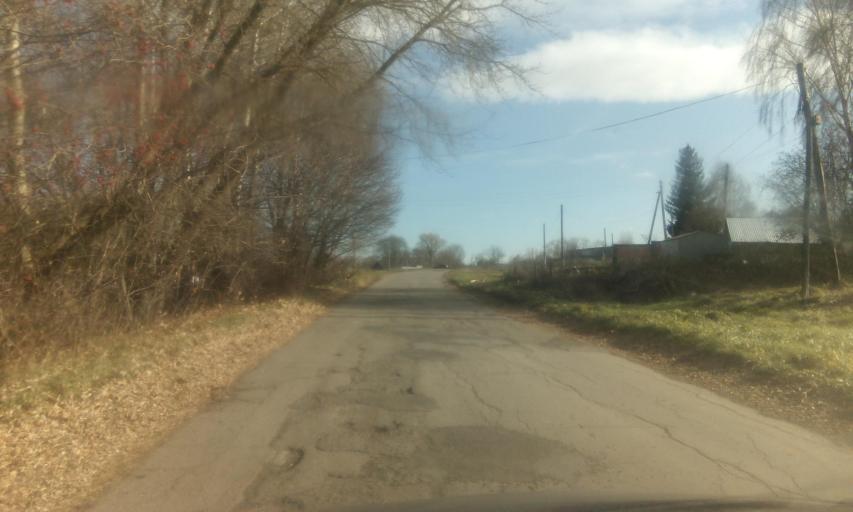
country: RU
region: Tula
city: Dubovka
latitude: 53.9464
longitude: 38.0325
